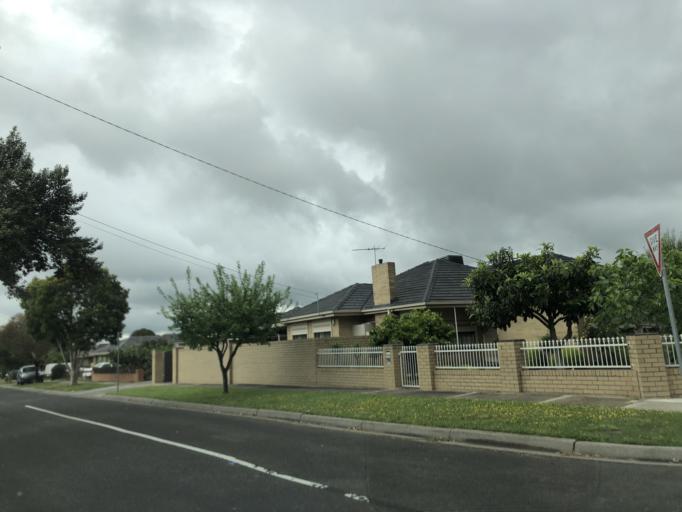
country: AU
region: Victoria
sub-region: Greater Dandenong
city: Dandenong North
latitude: -37.9561
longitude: 145.2076
